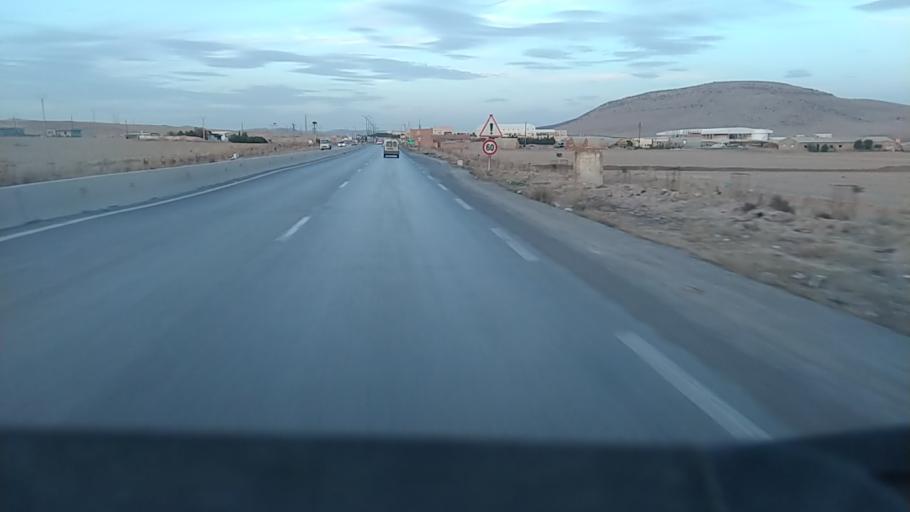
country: DZ
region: Oum el Bouaghi
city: Ain Kercha
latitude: 36.0772
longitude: 6.5882
